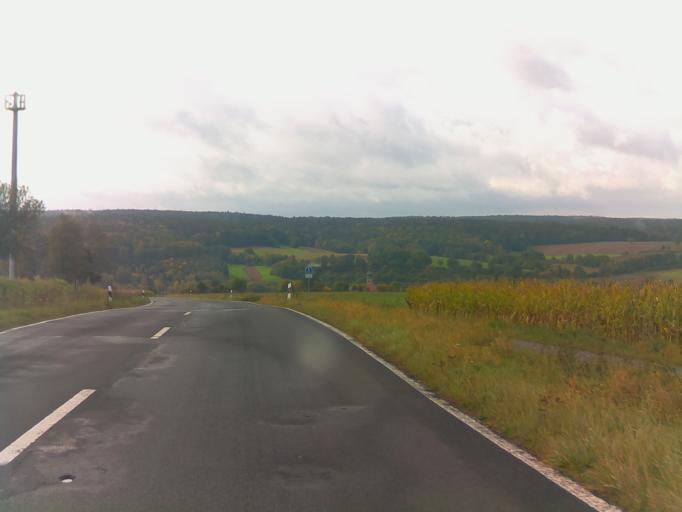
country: DE
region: Bavaria
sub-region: Upper Franconia
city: Burgwindheim
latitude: 49.8781
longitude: 10.6384
